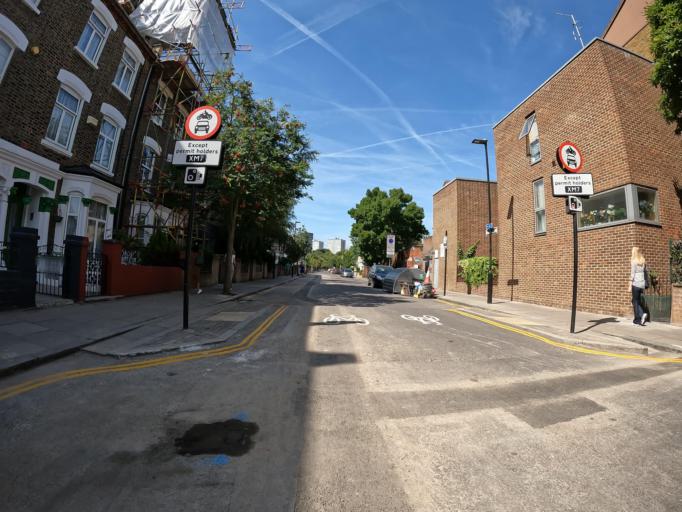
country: GB
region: England
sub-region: Greater London
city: Holloway
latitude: 51.5590
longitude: -0.1038
